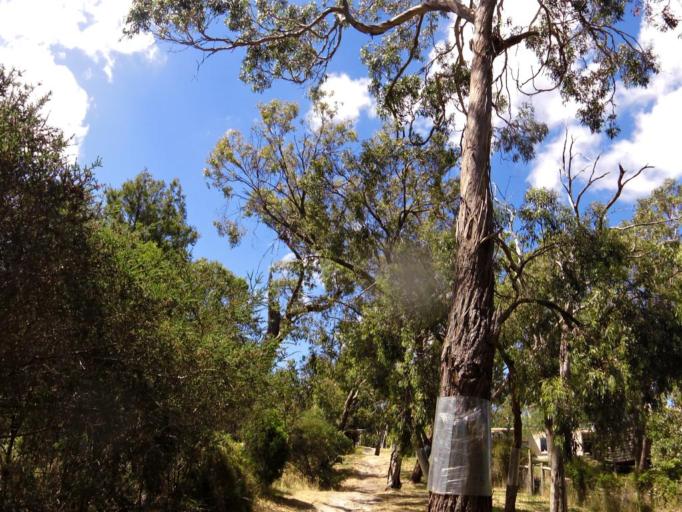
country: AU
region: Victoria
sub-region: Mornington Peninsula
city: Moorooduc
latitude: -38.2033
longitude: 145.1107
